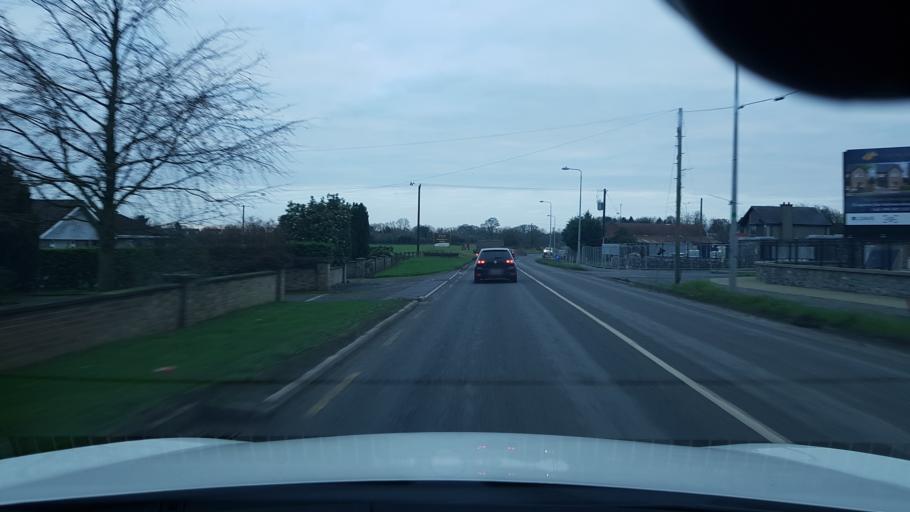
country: IE
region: Leinster
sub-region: An Mhi
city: Navan
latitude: 53.6734
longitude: -6.6774
